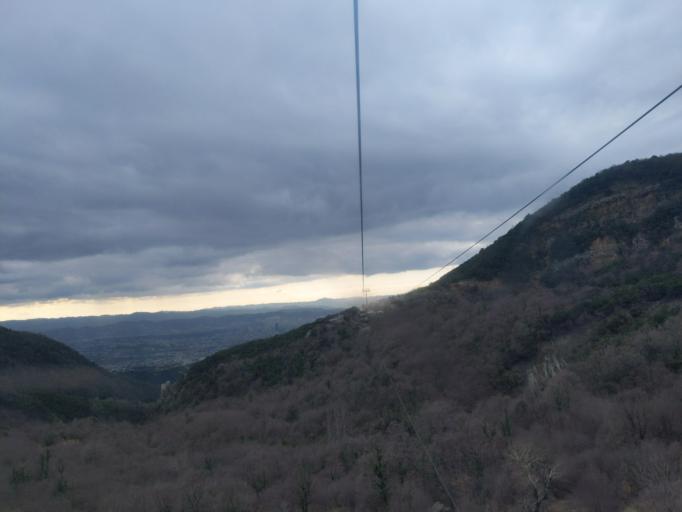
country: AL
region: Tirane
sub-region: Rrethi i Tiranes
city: Dajt
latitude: 41.3643
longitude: 19.8953
